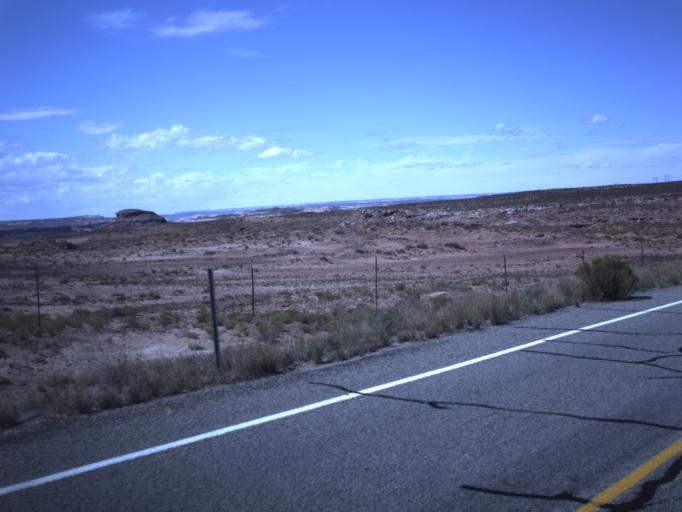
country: US
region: Utah
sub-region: San Juan County
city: Blanding
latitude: 37.2954
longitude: -109.4254
